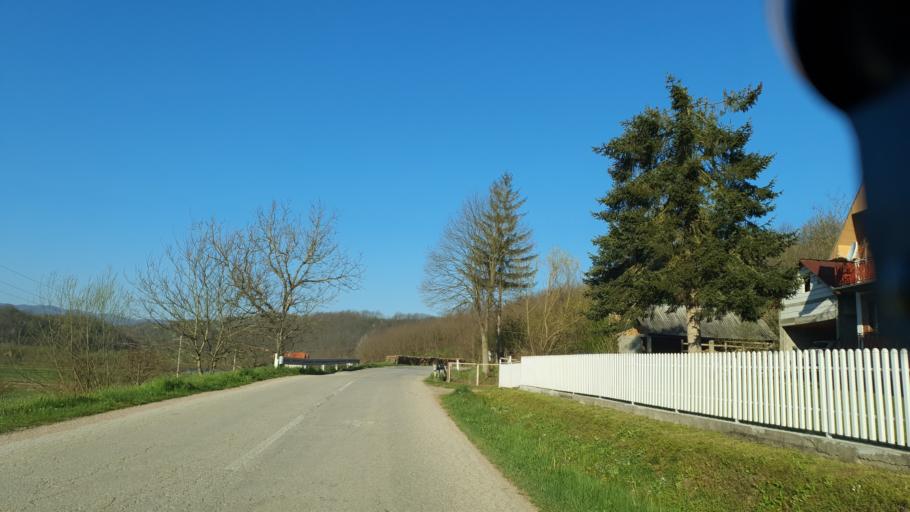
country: RS
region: Central Serbia
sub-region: Kolubarski Okrug
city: Osecina
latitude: 44.3580
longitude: 19.5344
